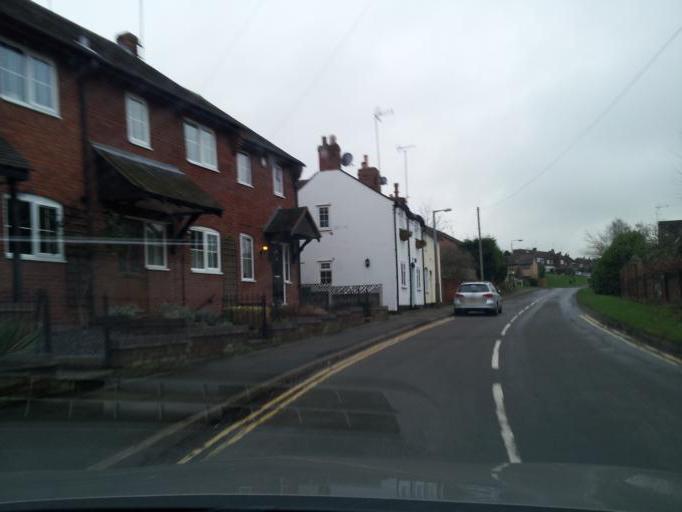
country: GB
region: England
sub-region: Derbyshire
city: Repton
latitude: 52.8361
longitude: -1.5443
